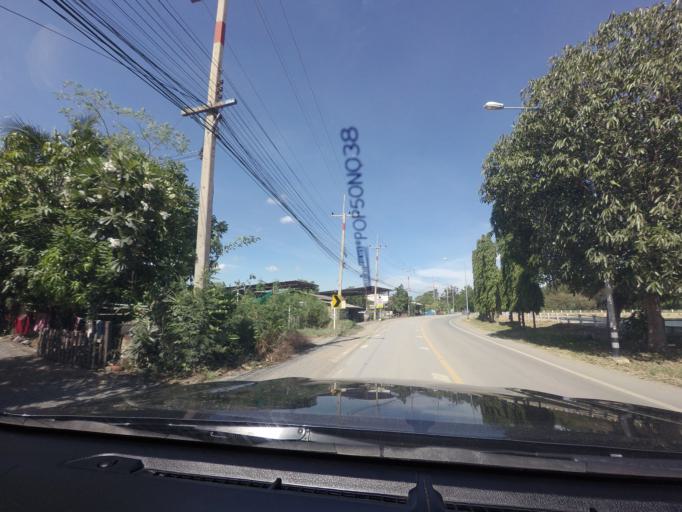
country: TH
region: Suphan Buri
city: Song Phi Nong
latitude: 14.1676
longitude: 100.0096
